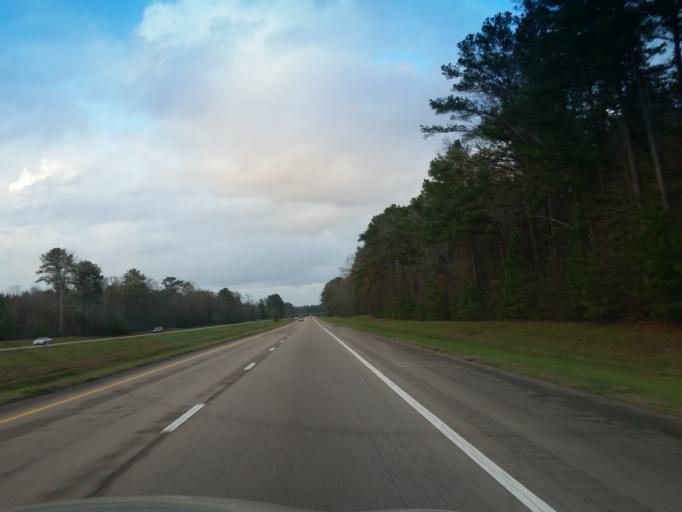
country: US
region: Mississippi
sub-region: Clarke County
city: Stonewall
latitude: 32.0297
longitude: -88.9220
